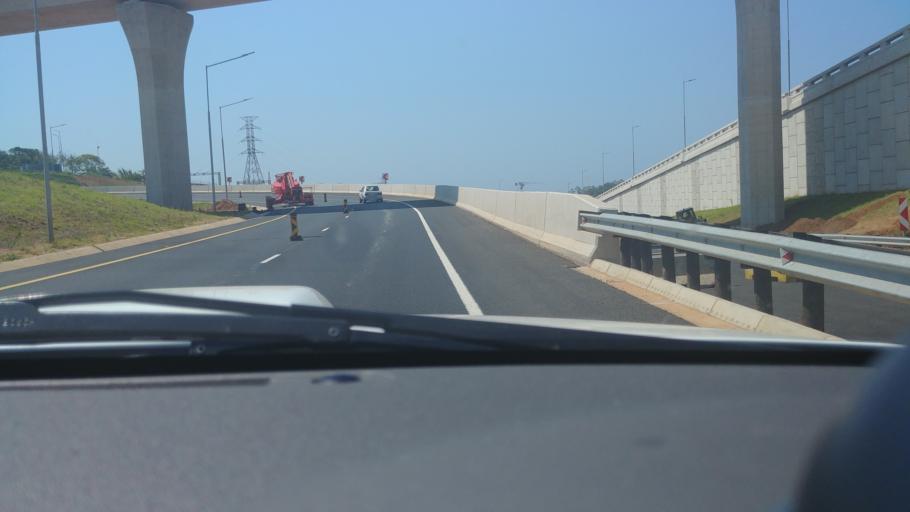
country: ZA
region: KwaZulu-Natal
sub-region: eThekwini Metropolitan Municipality
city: Durban
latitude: -29.7213
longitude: 31.0583
